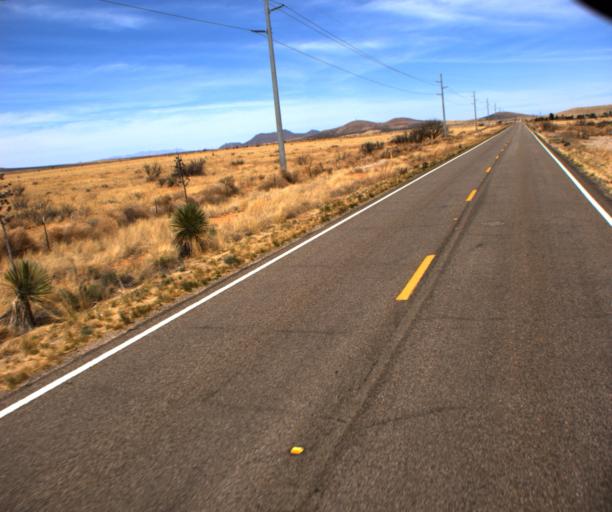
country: US
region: Arizona
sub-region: Cochise County
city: Tombstone
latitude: 31.8646
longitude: -109.6951
